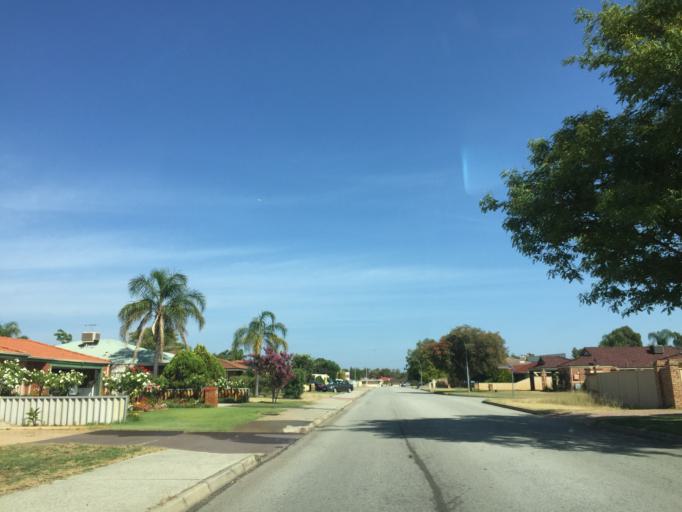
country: AU
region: Western Australia
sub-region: Gosnells
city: Thornlie
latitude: -32.0799
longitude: 115.9592
